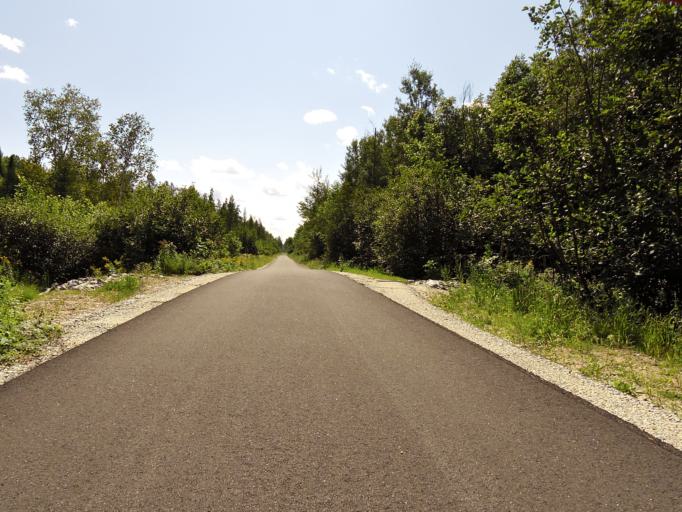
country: CA
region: Quebec
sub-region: Outaouais
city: Maniwaki
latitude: 46.1856
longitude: -76.0444
